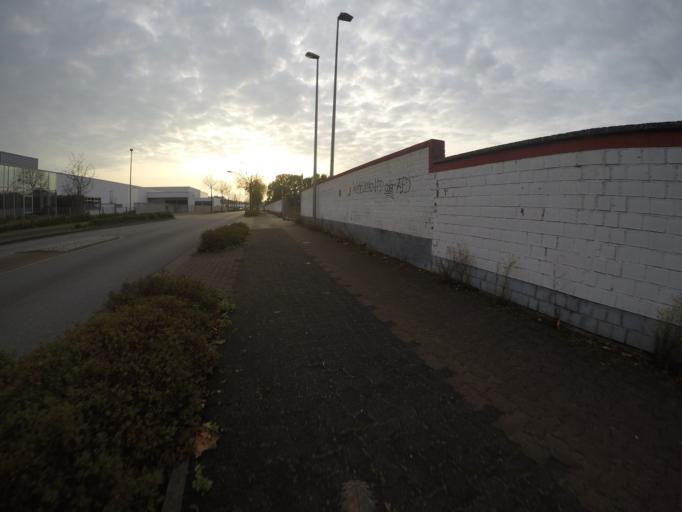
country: DE
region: North Rhine-Westphalia
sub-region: Regierungsbezirk Dusseldorf
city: Bocholt
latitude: 51.8267
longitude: 6.6287
